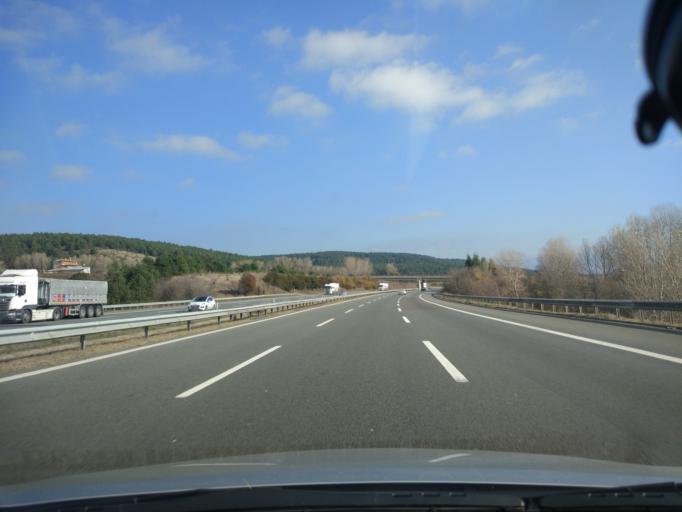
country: TR
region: Bolu
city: Bolu
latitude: 40.7794
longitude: 31.7081
